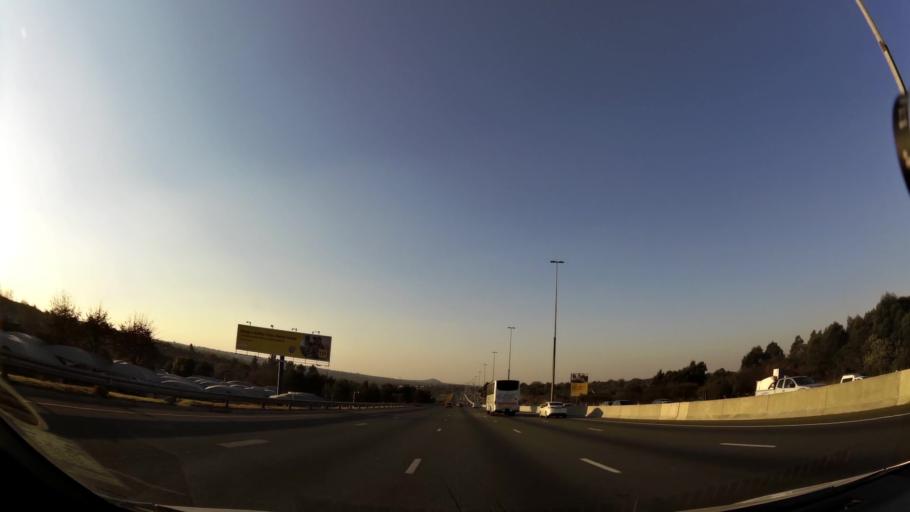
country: ZA
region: Gauteng
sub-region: City of Johannesburg Metropolitan Municipality
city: Roodepoort
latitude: -26.1465
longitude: 27.9298
